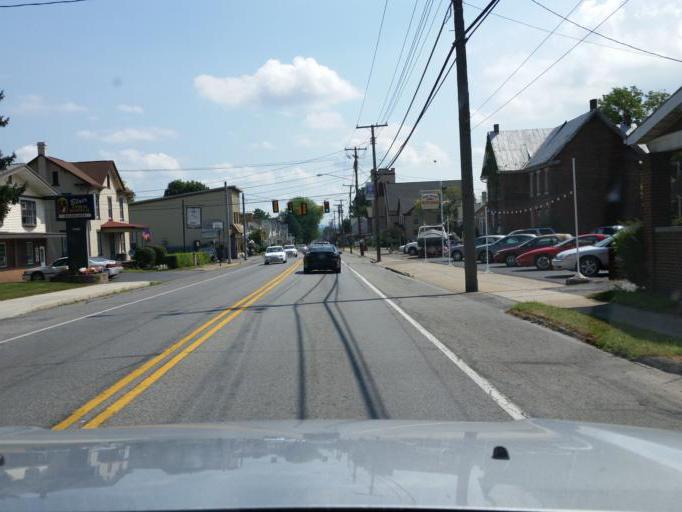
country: US
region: Pennsylvania
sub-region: Blair County
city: Duncansville
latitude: 40.4229
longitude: -78.4352
